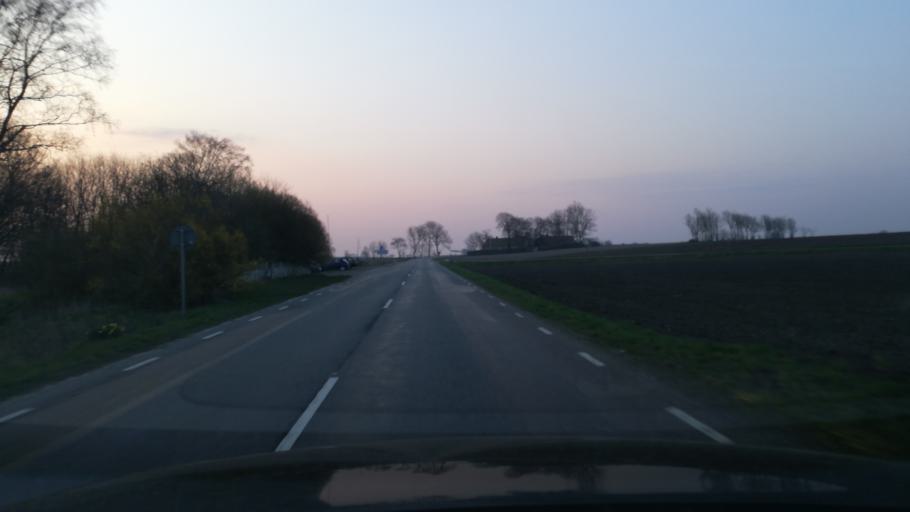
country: SE
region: Skane
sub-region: Tomelilla Kommun
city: Tomelilla
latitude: 55.4607
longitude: 14.1048
